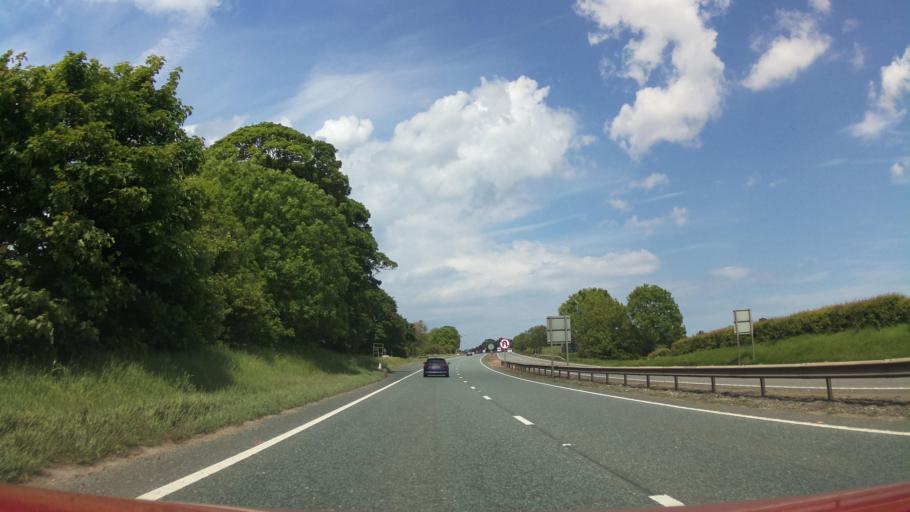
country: GB
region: England
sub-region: Hartlepool
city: Elwick
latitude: 54.6622
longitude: -1.3035
